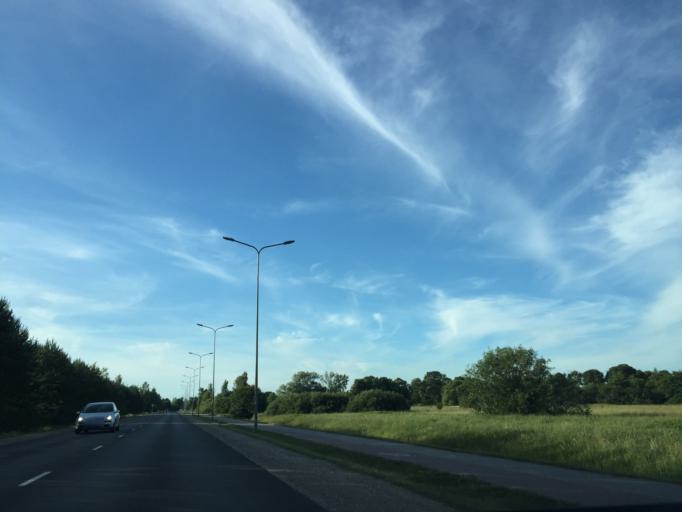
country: LV
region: Ventspils
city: Ventspils
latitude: 57.3558
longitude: 21.5638
